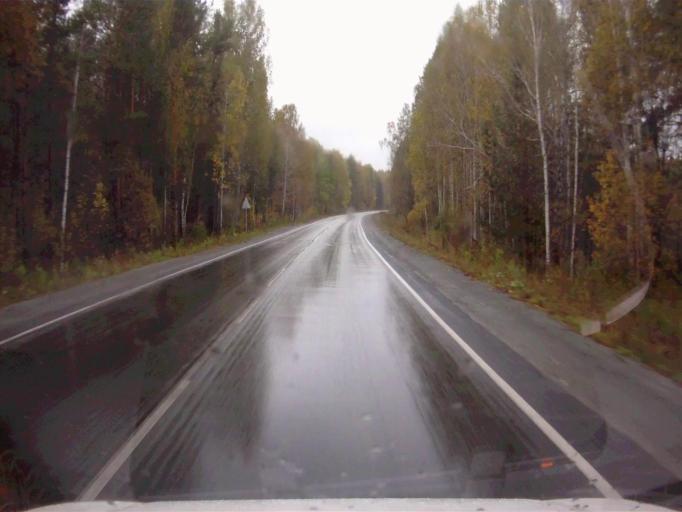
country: RU
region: Chelyabinsk
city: Tayginka
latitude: 55.5965
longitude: 60.6186
